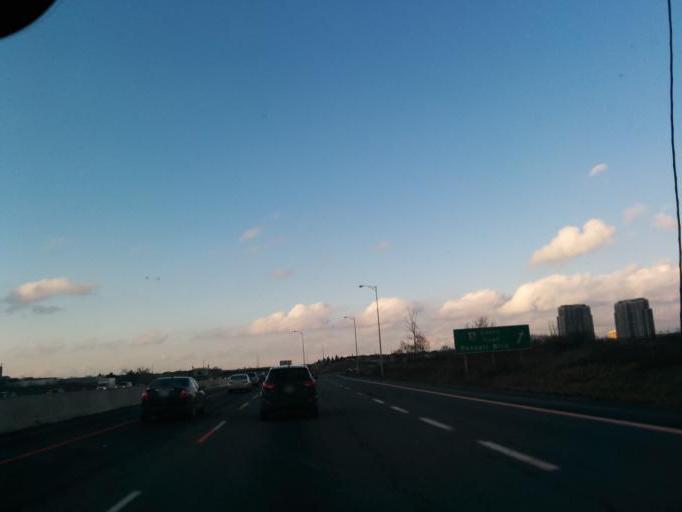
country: CA
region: Ontario
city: Etobicoke
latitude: 43.7142
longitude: -79.6177
